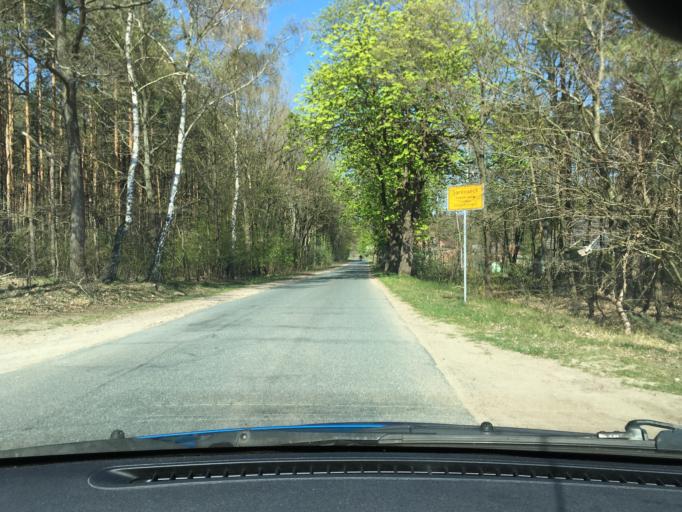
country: DE
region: Lower Saxony
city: Karwitz
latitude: 53.1231
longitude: 11.0107
